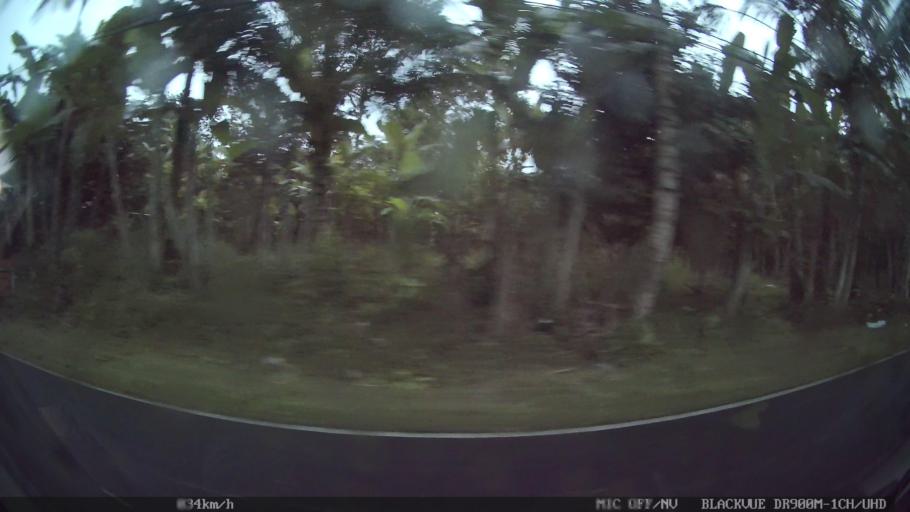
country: ID
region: Bali
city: Banjar Taro Kelod
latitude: -8.3626
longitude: 115.2714
